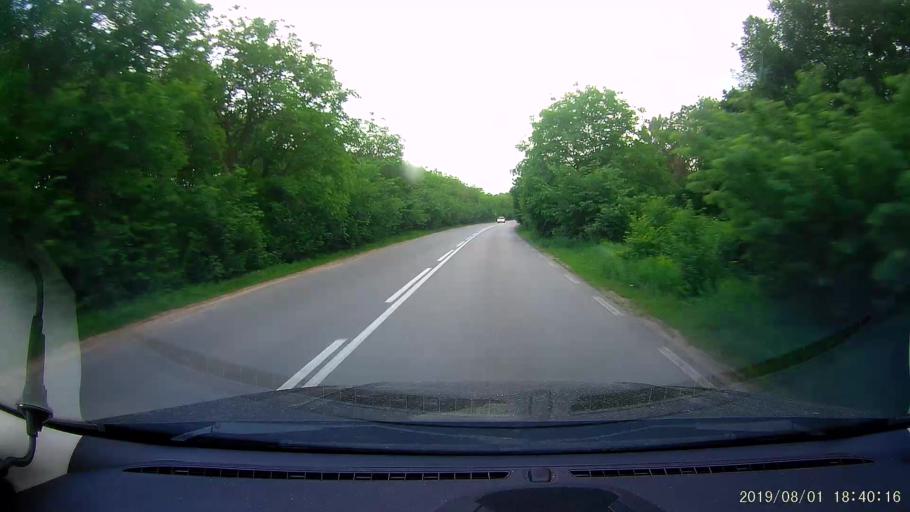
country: BG
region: Shumen
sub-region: Obshtina Khitrino
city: Gara Khitrino
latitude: 43.3705
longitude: 26.9199
